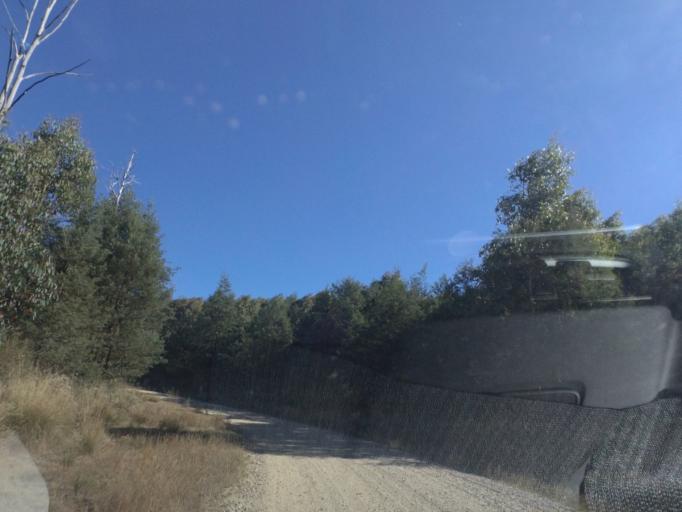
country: AU
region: Victoria
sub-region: Murrindindi
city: Alexandra
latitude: -37.4092
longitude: 145.8072
